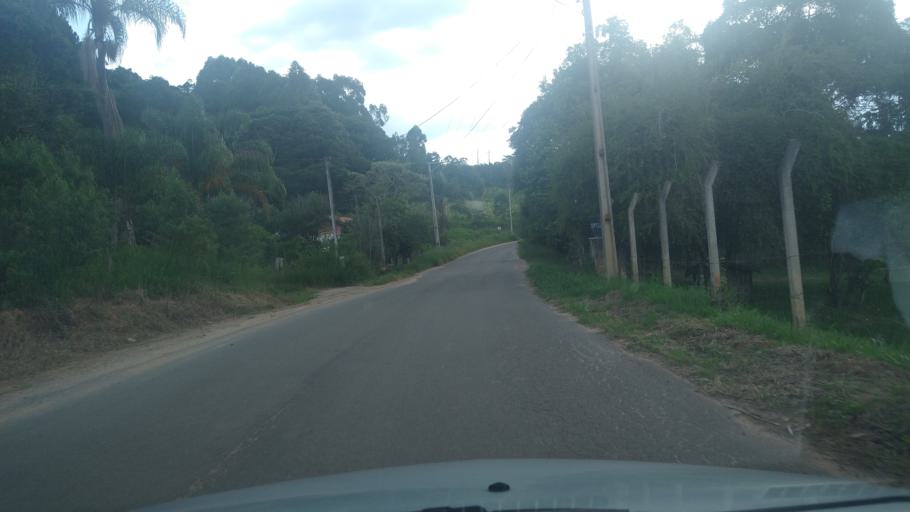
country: BR
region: Minas Gerais
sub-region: Extrema
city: Extrema
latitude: -22.7203
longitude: -46.3409
